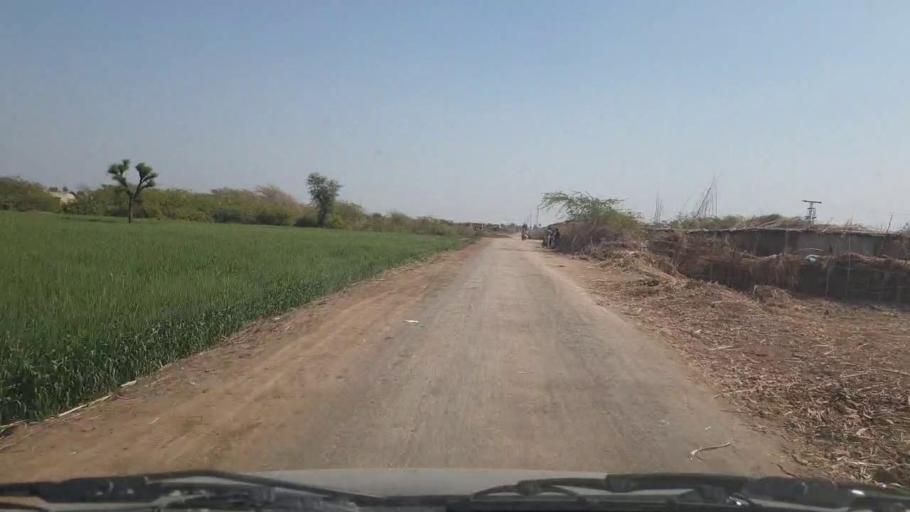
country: PK
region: Sindh
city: Samaro
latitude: 25.2487
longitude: 69.3614
